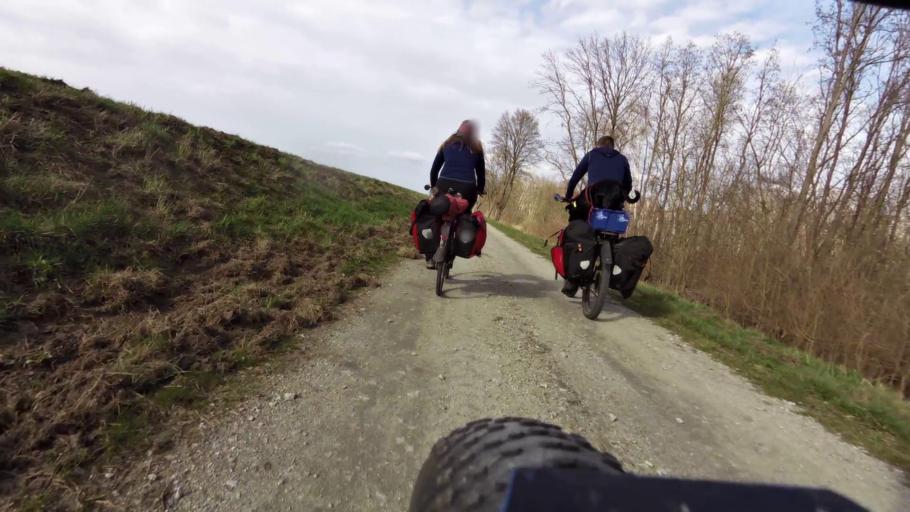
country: DE
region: Brandenburg
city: Reitwein
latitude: 52.5266
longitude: 14.6104
